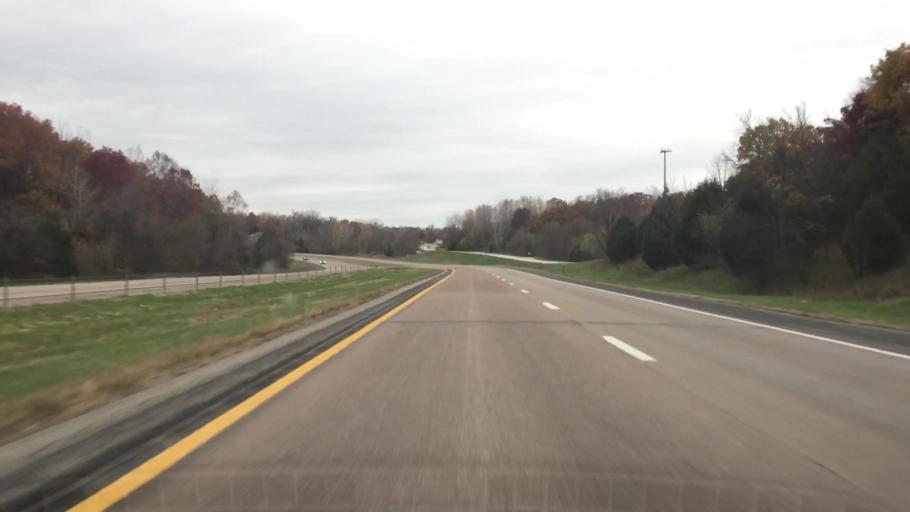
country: US
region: Missouri
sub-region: Cole County
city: Jefferson City
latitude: 38.6657
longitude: -92.2275
